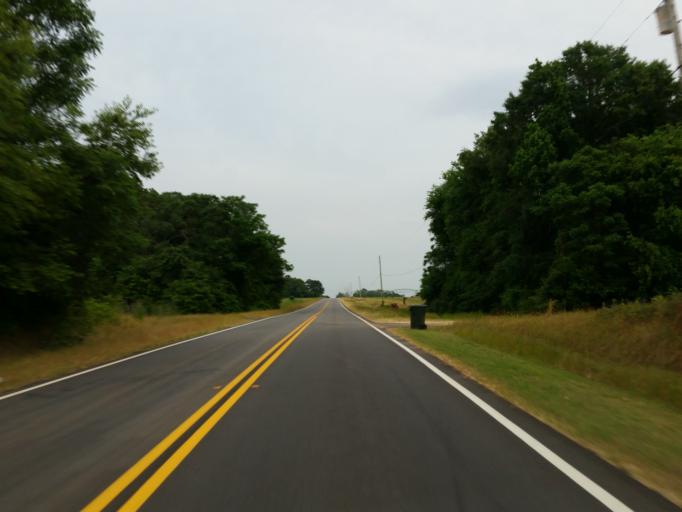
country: US
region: Georgia
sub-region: Dooly County
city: Unadilla
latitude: 32.3166
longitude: -83.7740
